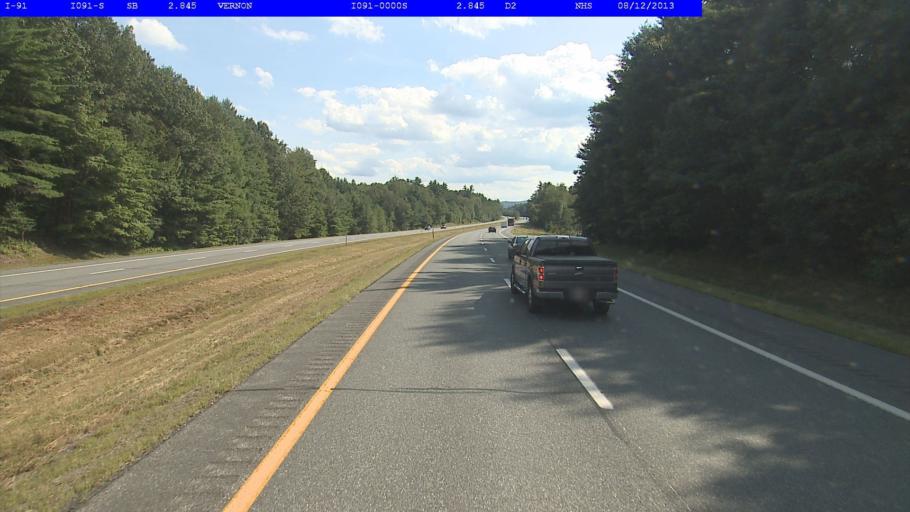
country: US
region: New Hampshire
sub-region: Cheshire County
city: Hinsdale
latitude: 42.7707
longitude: -72.5619
